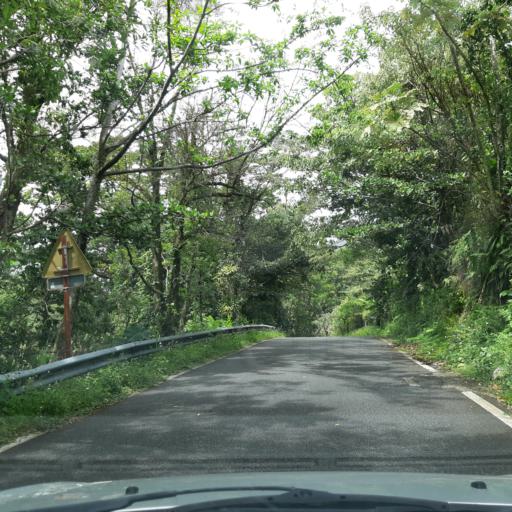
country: GP
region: Guadeloupe
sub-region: Guadeloupe
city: Saint-Claude
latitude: 16.0323
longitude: -61.6826
